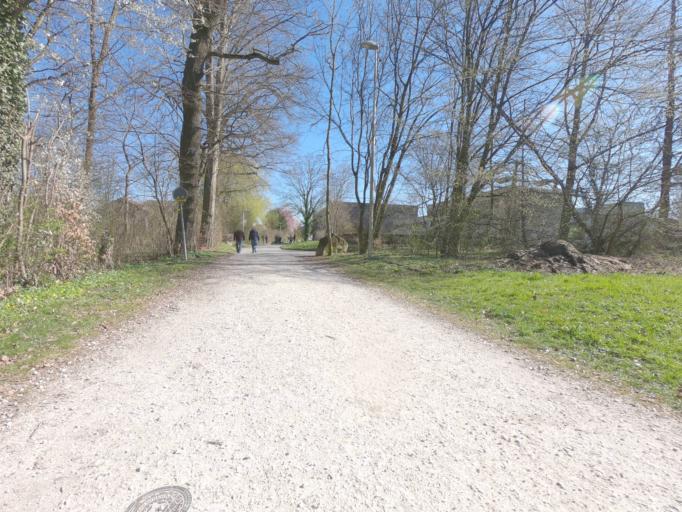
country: CH
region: Solothurn
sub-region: Bezirk Wasseramt
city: Zuchwil
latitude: 47.2125
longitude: 7.5561
